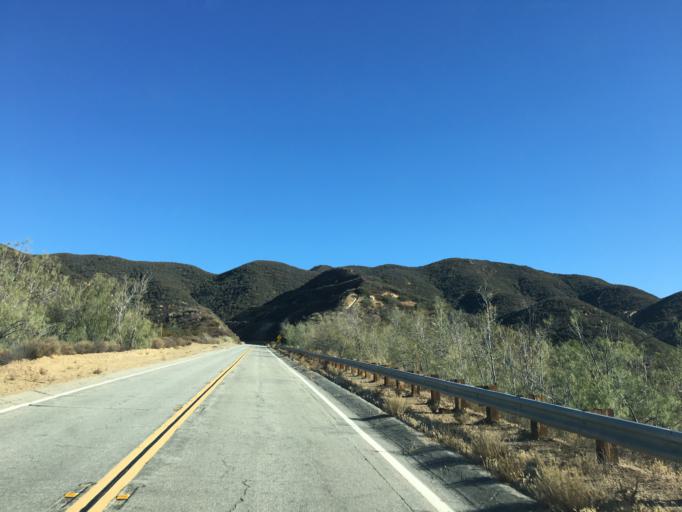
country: US
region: California
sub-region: Los Angeles County
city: Castaic
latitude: 34.5578
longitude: -118.5420
